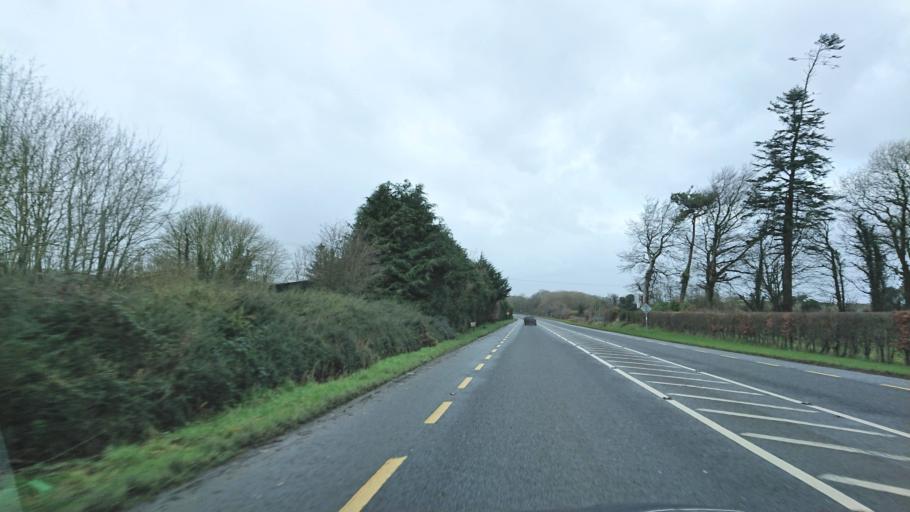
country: IE
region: Leinster
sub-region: Loch Garman
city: New Ross
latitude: 52.3802
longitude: -6.8614
